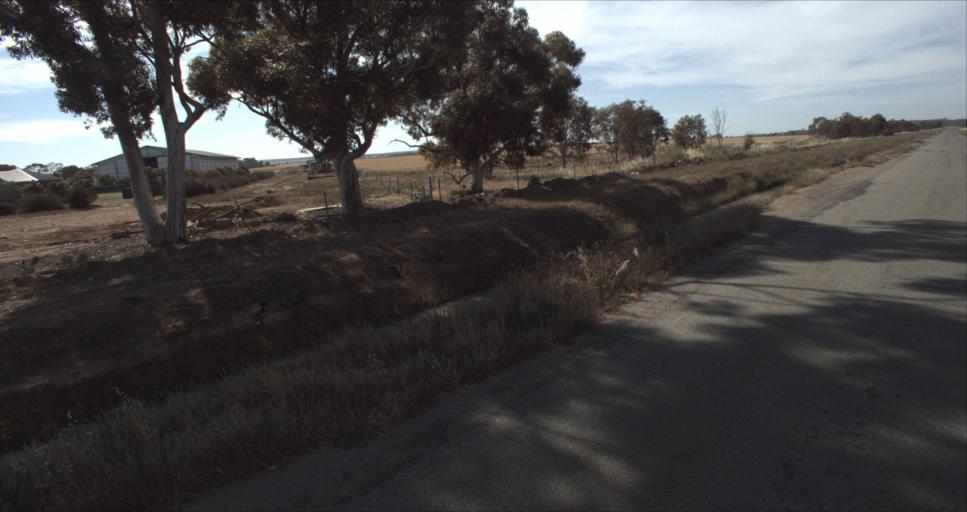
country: AU
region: New South Wales
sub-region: Leeton
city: Leeton
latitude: -34.5598
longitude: 146.4681
